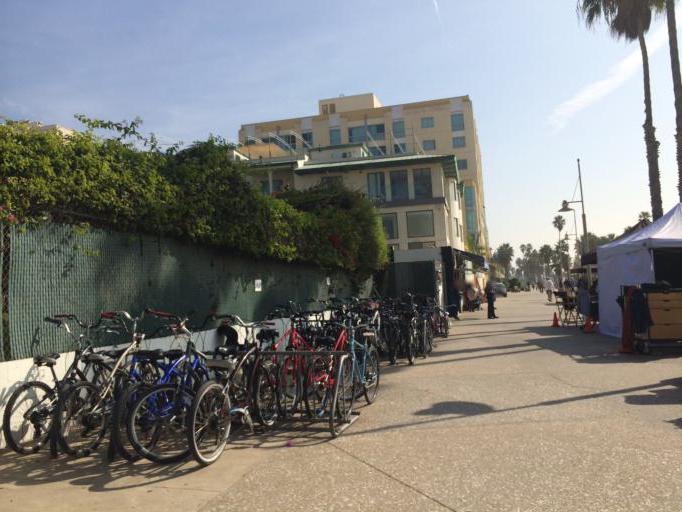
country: US
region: California
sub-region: Los Angeles County
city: Santa Monica
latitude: 34.0087
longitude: -118.4940
